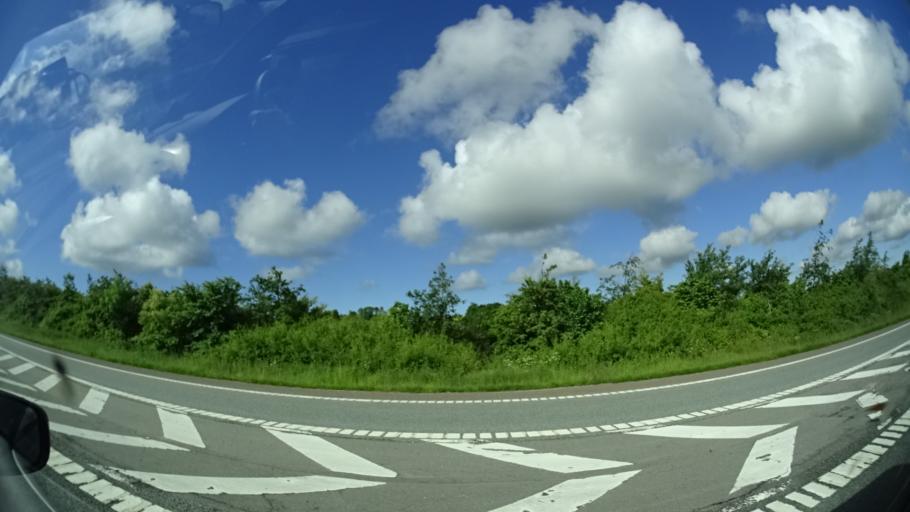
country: DK
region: Central Jutland
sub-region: Syddjurs Kommune
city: Ronde
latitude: 56.3057
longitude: 10.5043
